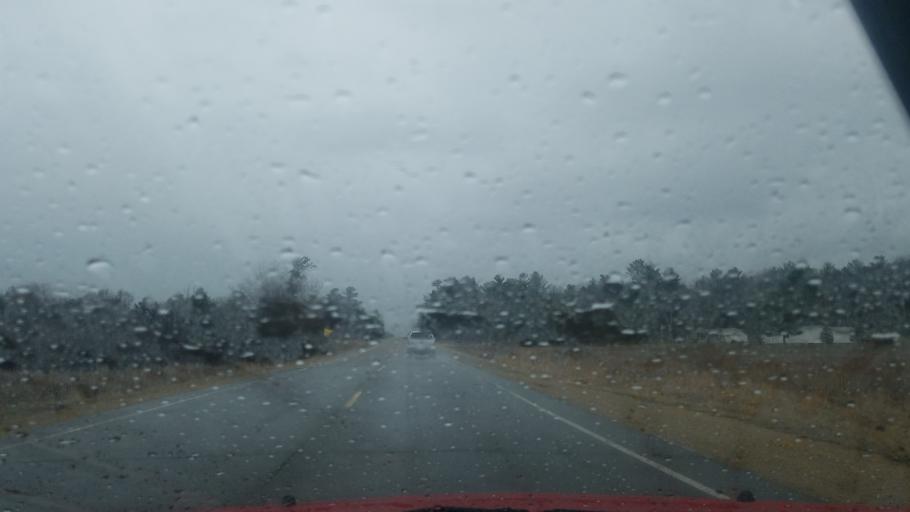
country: US
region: Wisconsin
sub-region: Dunn County
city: Tainter Lake
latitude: 44.9711
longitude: -91.8942
